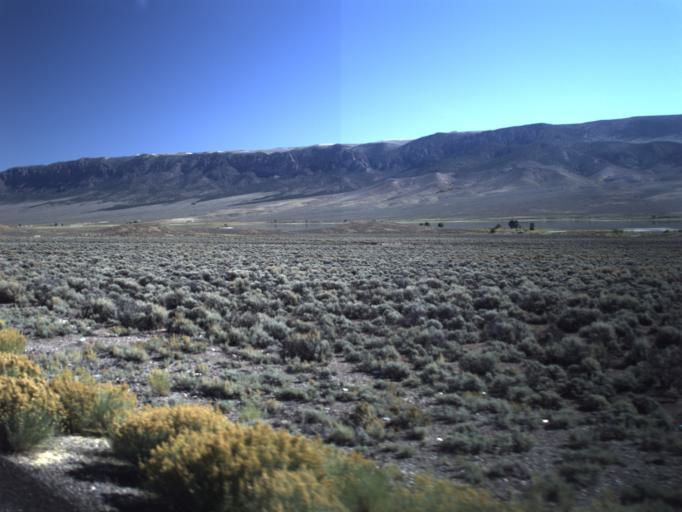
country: US
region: Utah
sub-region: Piute County
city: Junction
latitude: 38.2035
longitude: -112.0069
